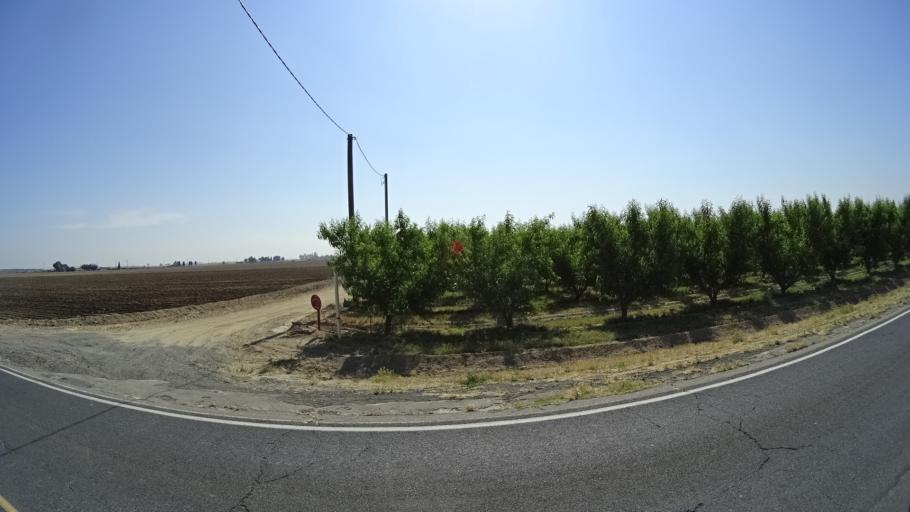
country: US
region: California
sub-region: Kings County
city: Lucerne
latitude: 36.3976
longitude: -119.5650
